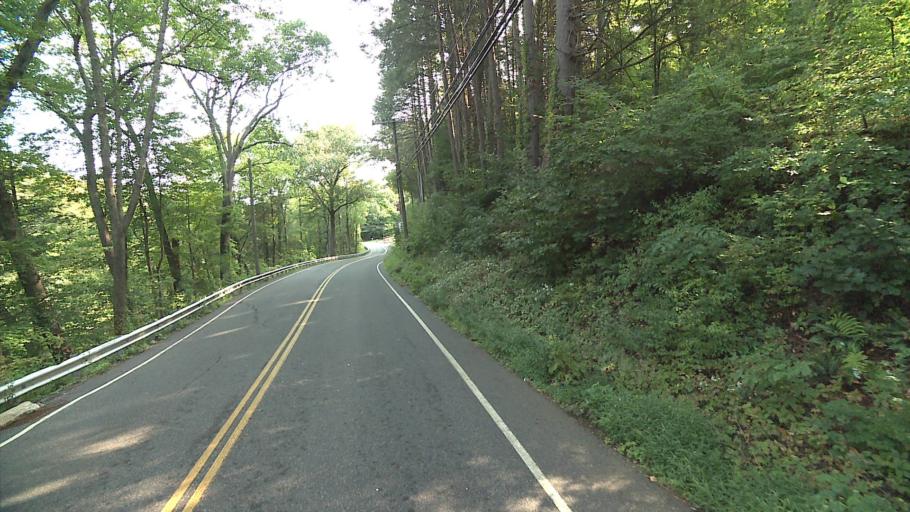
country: US
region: Connecticut
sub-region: Fairfield County
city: Newtown
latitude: 41.4304
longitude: -73.2776
